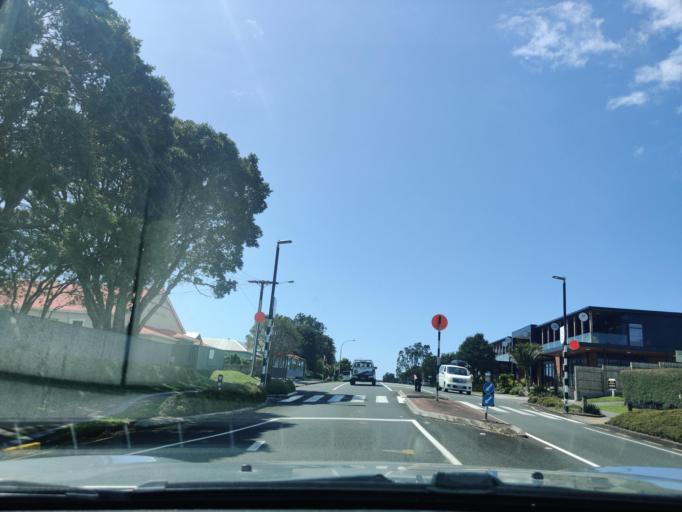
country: NZ
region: Taranaki
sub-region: New Plymouth District
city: New Plymouth
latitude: -39.1180
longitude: 173.9559
